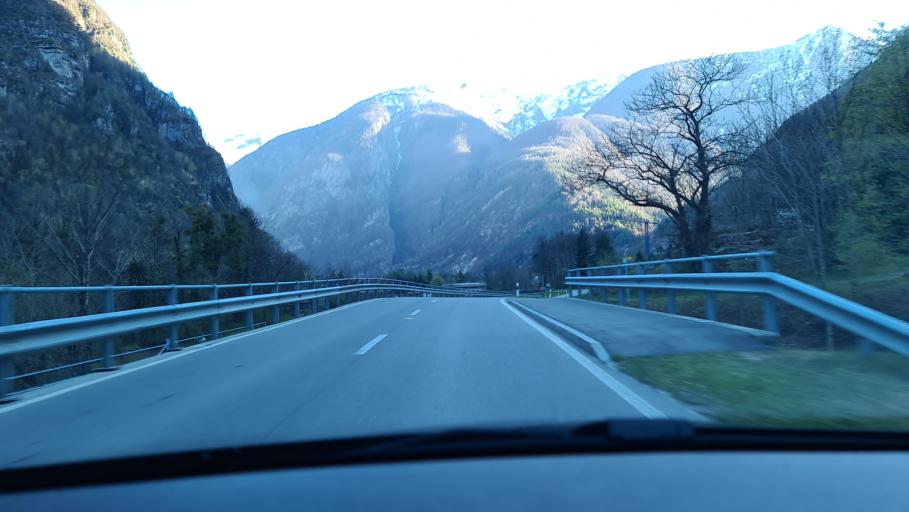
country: CH
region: Ticino
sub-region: Vallemaggia District
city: Cevio
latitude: 46.3292
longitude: 8.6066
